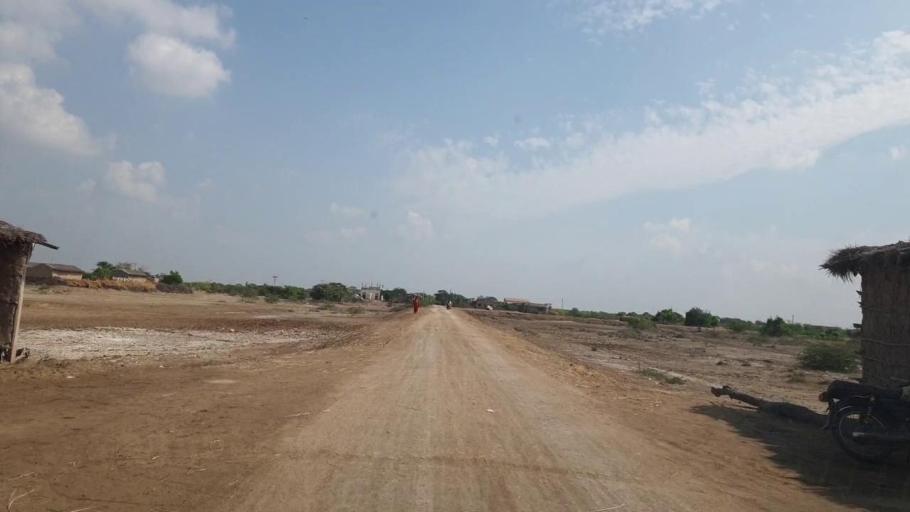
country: PK
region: Sindh
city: Badin
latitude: 24.4784
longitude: 68.6086
